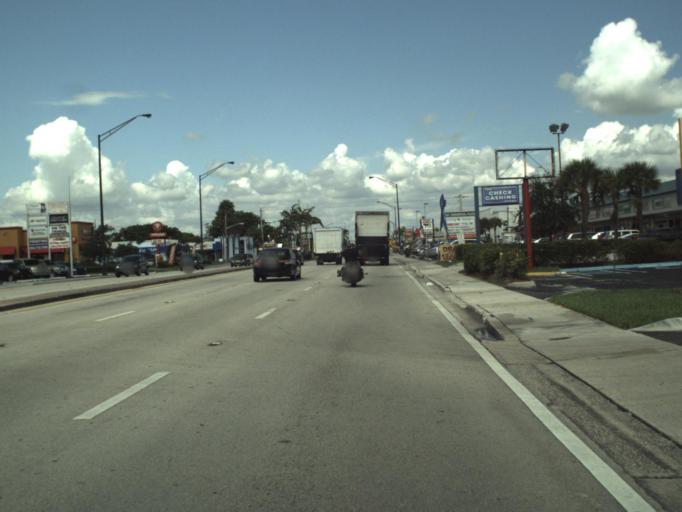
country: US
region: Florida
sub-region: Broward County
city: North Andrews Gardens
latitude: 26.1891
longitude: -80.1285
